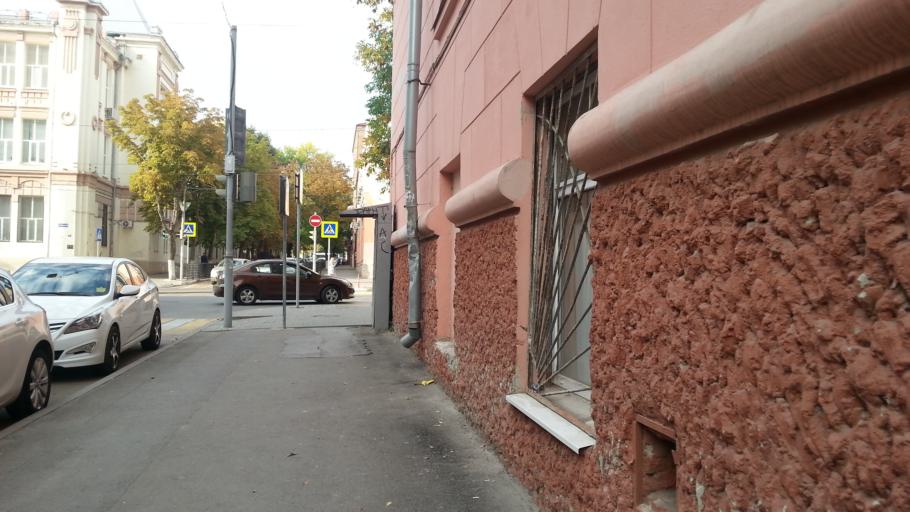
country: RU
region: Rostov
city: Rostov-na-Donu
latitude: 47.2250
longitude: 39.7087
